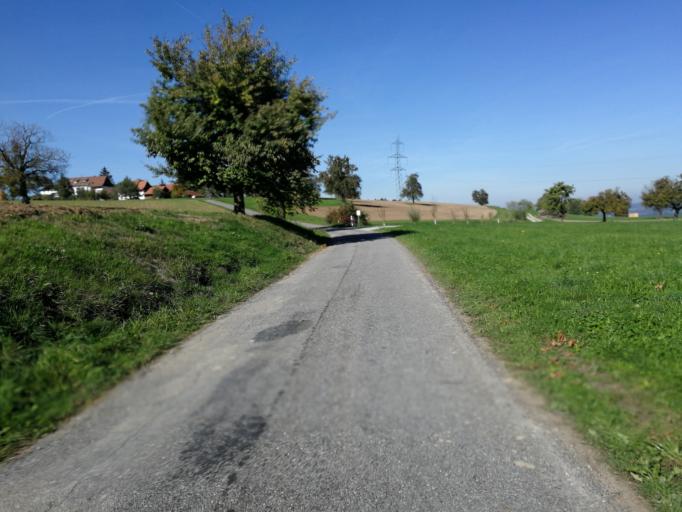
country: CH
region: Zurich
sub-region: Bezirk Uster
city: Hinteregg
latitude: 47.3114
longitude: 8.6802
